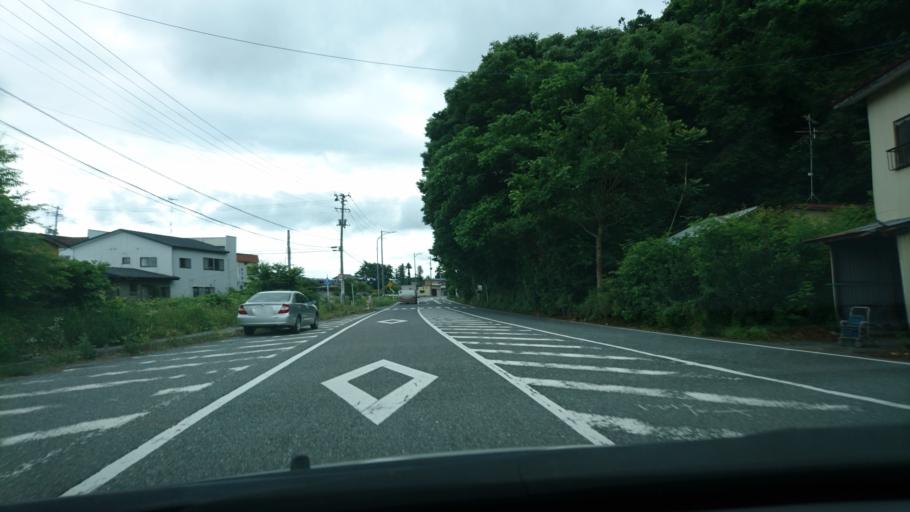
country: JP
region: Iwate
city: Ichinoseki
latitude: 38.7329
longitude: 141.2597
